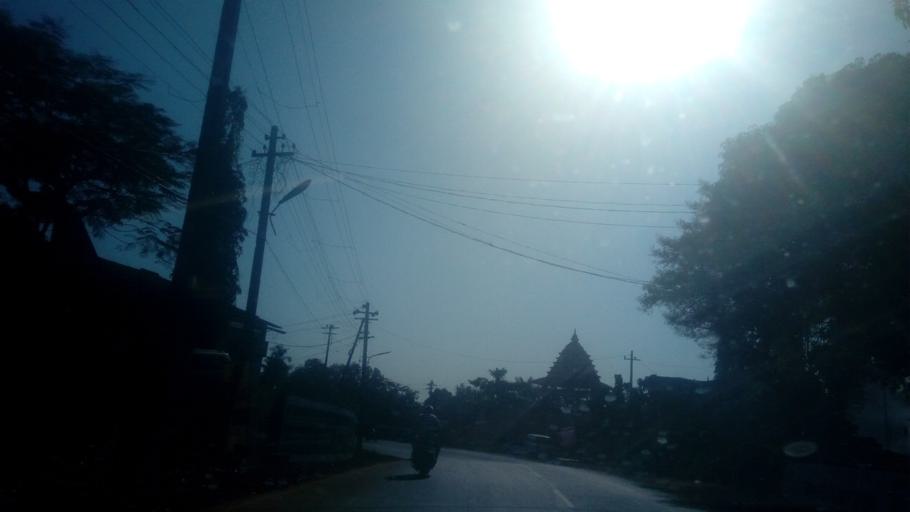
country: IN
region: Goa
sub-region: North Goa
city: Jua
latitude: 15.5129
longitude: 73.9606
